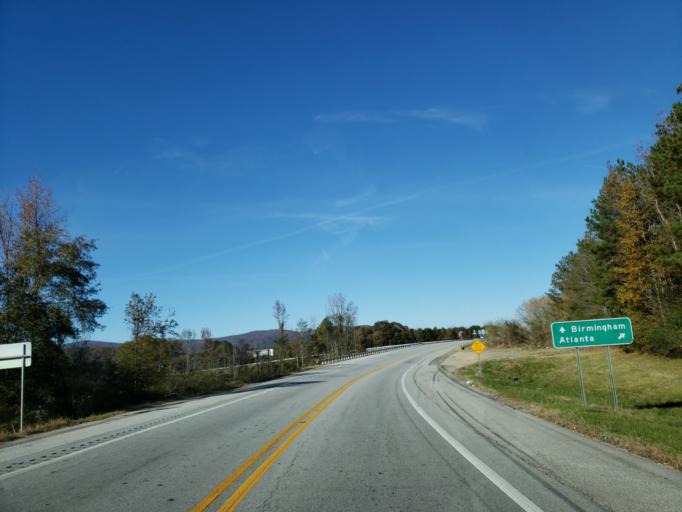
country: US
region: Alabama
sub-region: Calhoun County
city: Choccolocco
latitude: 33.6147
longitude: -85.7235
